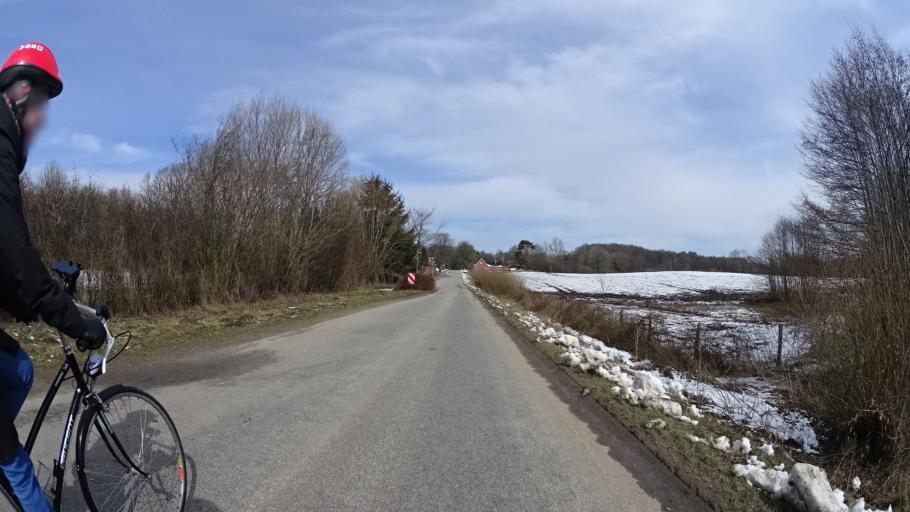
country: DE
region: Schleswig-Holstein
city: Stolpe
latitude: 54.1372
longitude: 10.2260
